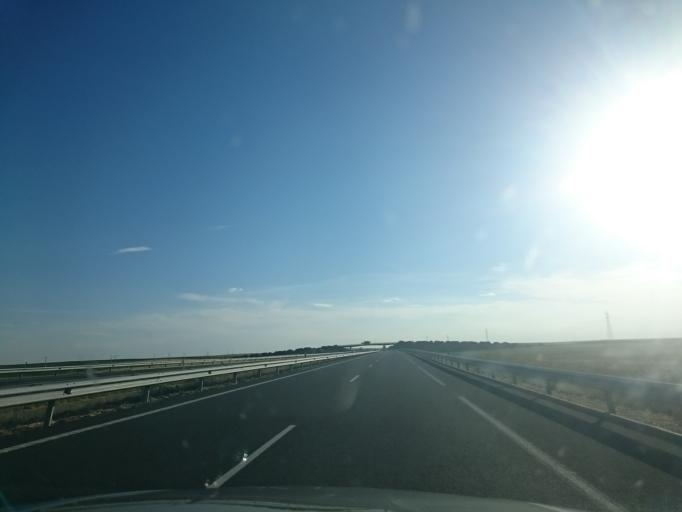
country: ES
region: Castille and Leon
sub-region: Provincia de Palencia
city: Villasarracino
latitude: 42.3844
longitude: -4.4930
